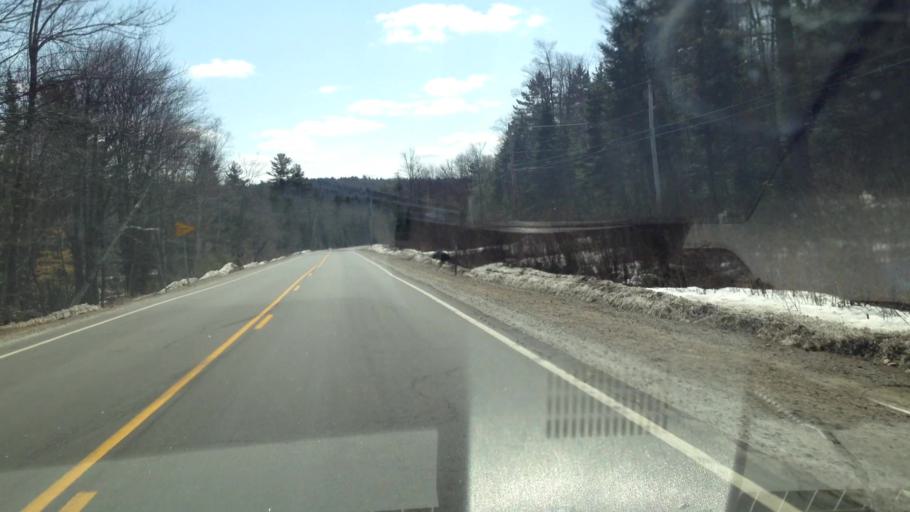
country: US
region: New Hampshire
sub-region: Merrimack County
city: Wilmot
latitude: 43.4717
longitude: -71.9624
